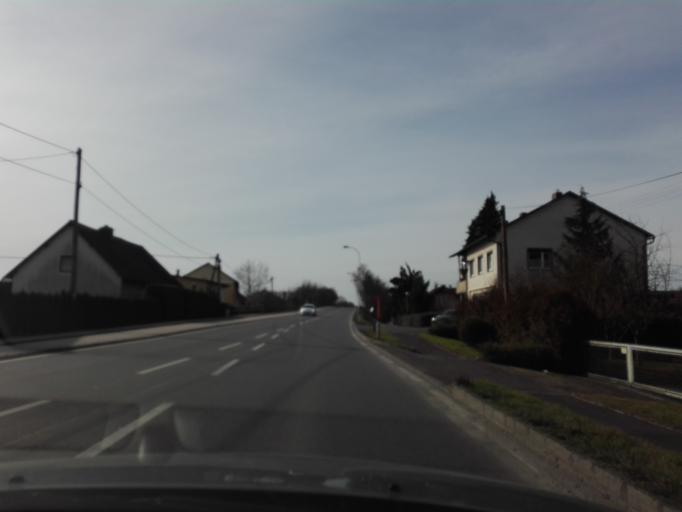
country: AT
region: Upper Austria
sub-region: Politischer Bezirk Linz-Land
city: Ansfelden
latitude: 48.2286
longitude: 14.3028
